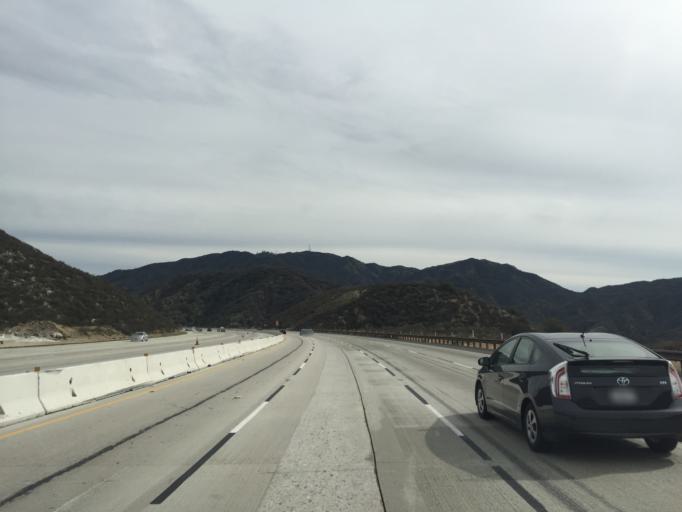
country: US
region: California
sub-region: Los Angeles County
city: Burbank
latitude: 34.2451
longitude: -118.3201
